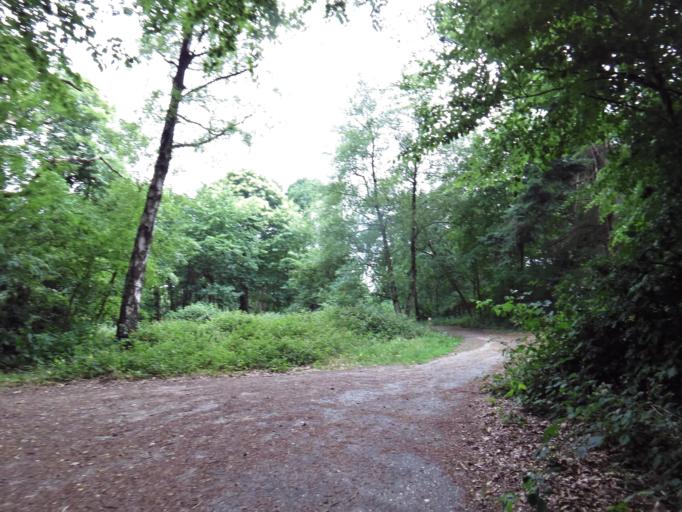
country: NL
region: North Brabant
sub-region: Gemeente Cuijk
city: Cuijk
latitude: 51.7678
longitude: 5.8887
